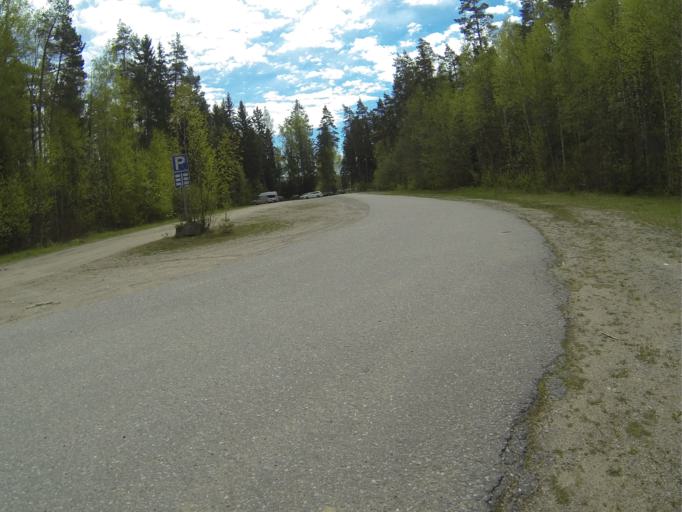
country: FI
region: Varsinais-Suomi
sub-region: Salo
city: Halikko
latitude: 60.3020
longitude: 23.0764
